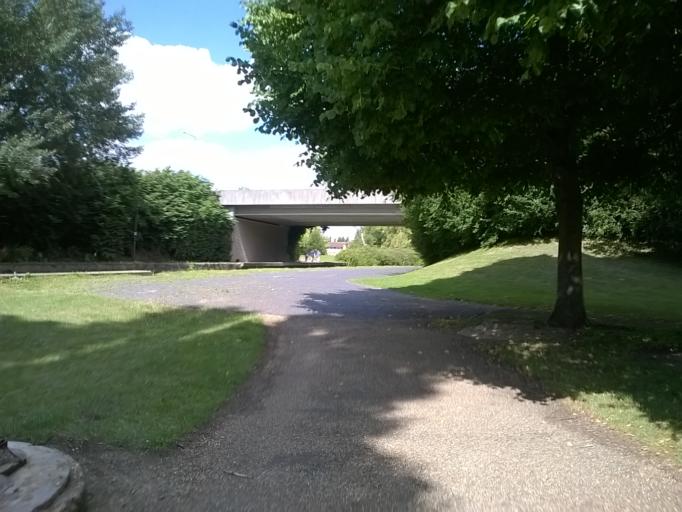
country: GB
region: England
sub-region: Milton Keynes
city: Milton Keynes
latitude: 52.0608
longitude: -0.7381
